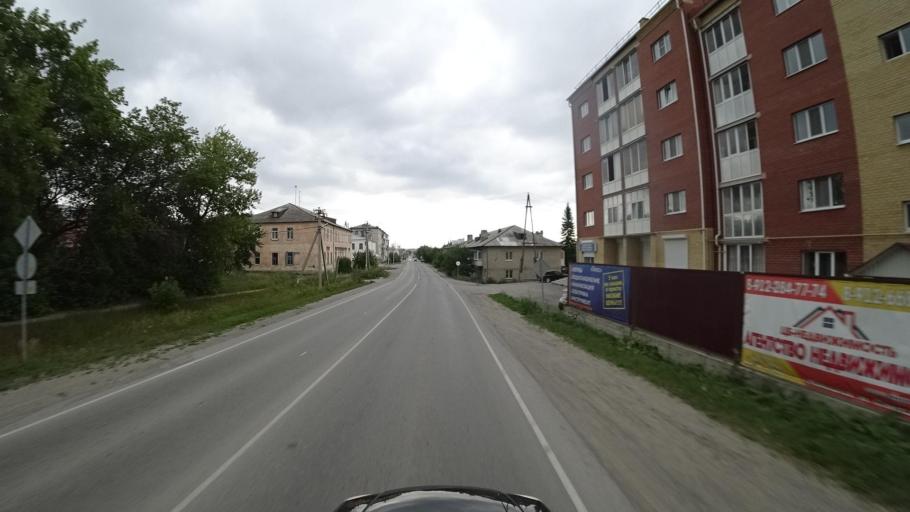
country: RU
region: Sverdlovsk
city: Kamyshlov
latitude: 56.8455
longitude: 62.6904
